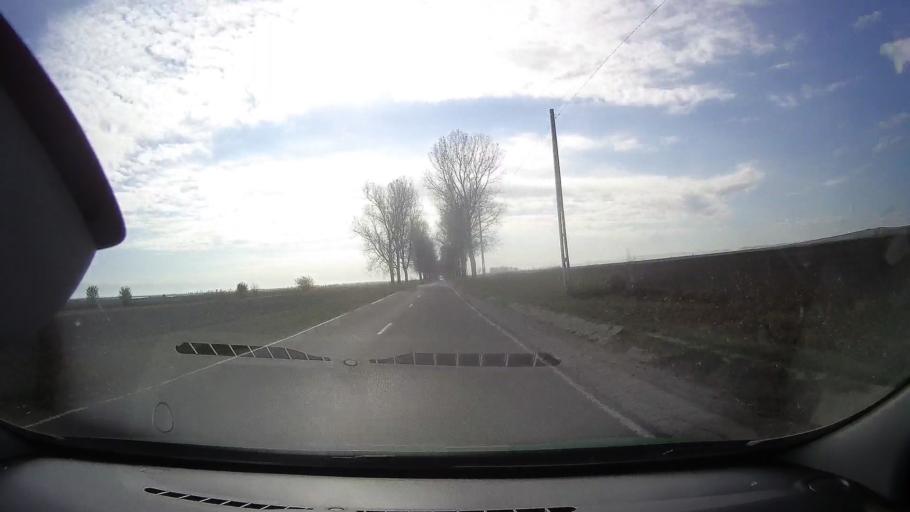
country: RO
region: Tulcea
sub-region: Comuna Valea Nucarilor
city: Agighiol
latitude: 45.0071
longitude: 28.8849
